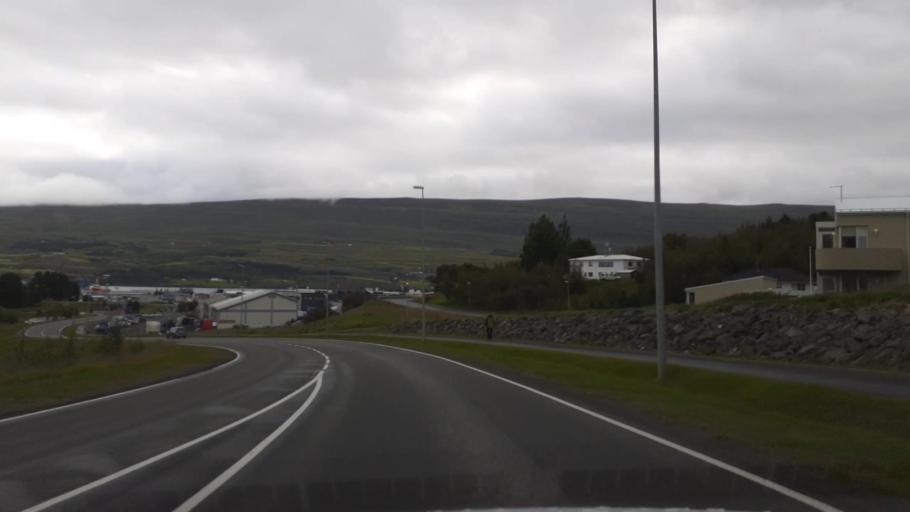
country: IS
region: Northeast
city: Akureyri
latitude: 65.6855
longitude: -18.1116
